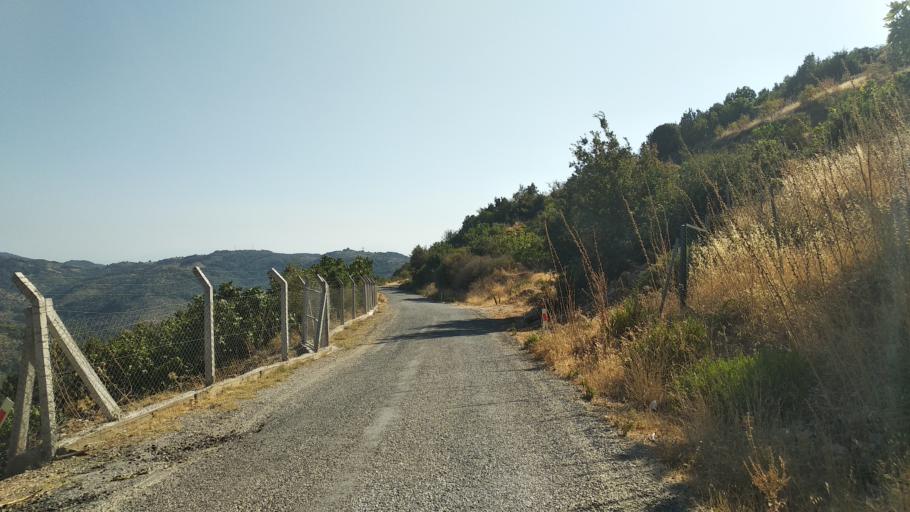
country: TR
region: Izmir
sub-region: Seferihisar
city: Seferhisar
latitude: 38.3207
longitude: 26.9297
